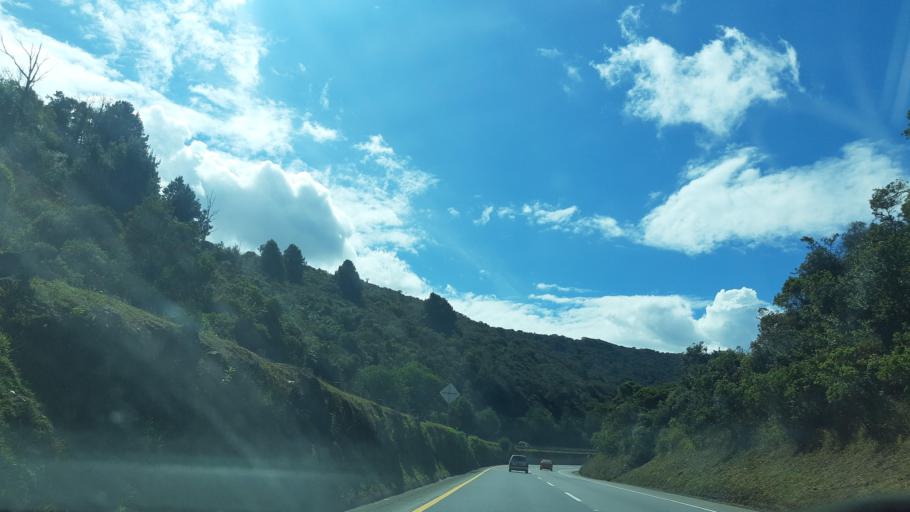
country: CO
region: Cundinamarca
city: Suesca
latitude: 5.0824
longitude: -73.7279
